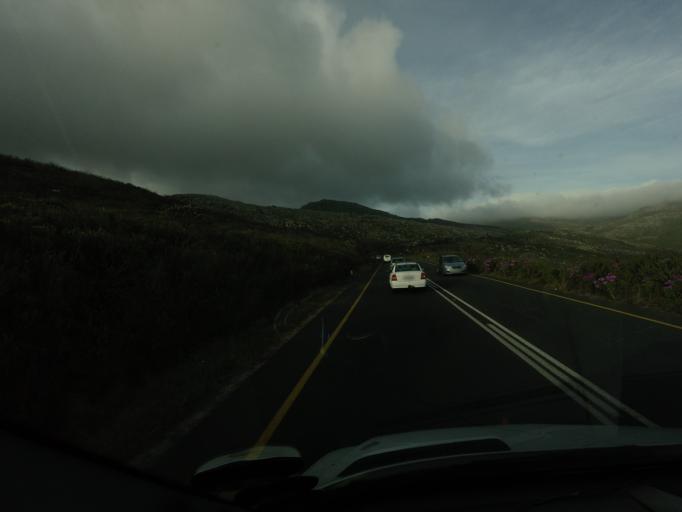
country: ZA
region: Western Cape
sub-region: City of Cape Town
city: Bergvliet
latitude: -34.1024
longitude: 18.4084
